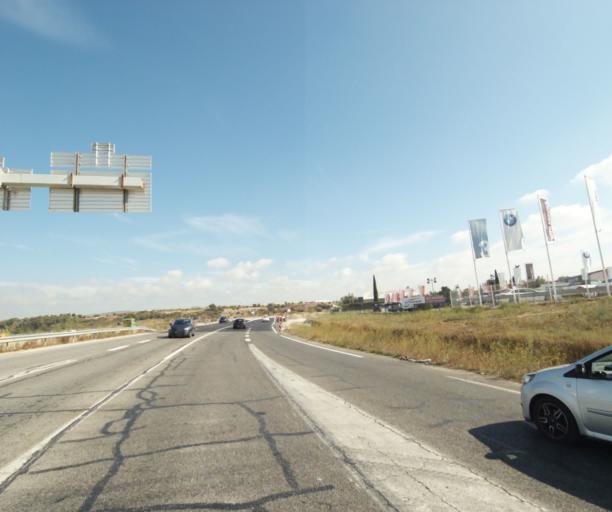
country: FR
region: Provence-Alpes-Cote d'Azur
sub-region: Departement des Bouches-du-Rhone
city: Saint-Victoret
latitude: 43.4226
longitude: 5.2296
